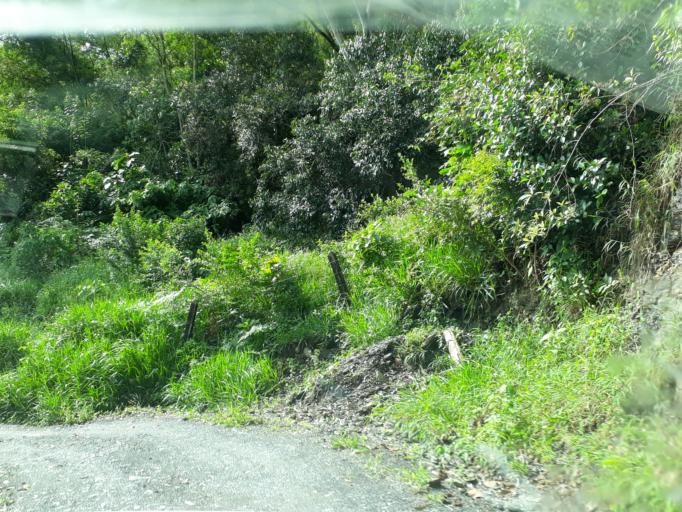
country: CO
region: Cundinamarca
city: Pacho
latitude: 5.1697
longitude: -74.2422
